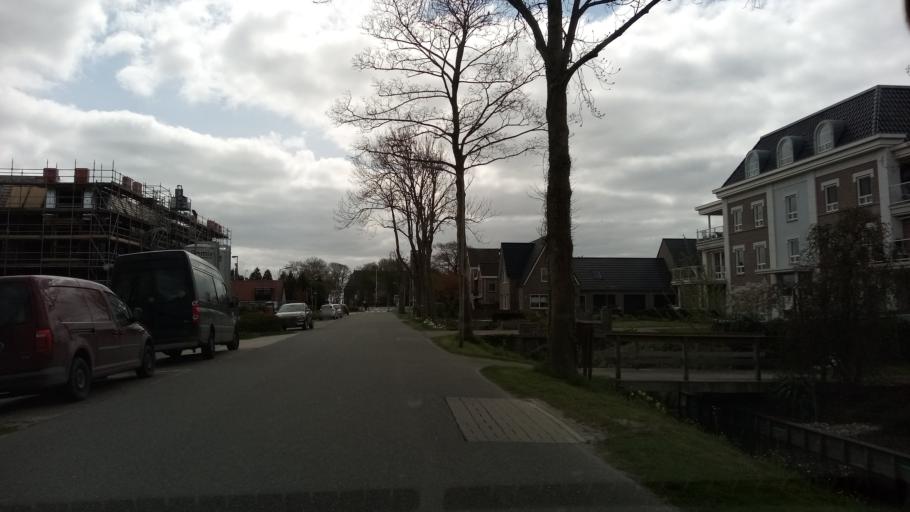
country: NL
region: North Holland
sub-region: Gemeente Langedijk
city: Broek op Langedijk
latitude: 52.6135
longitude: 4.8208
